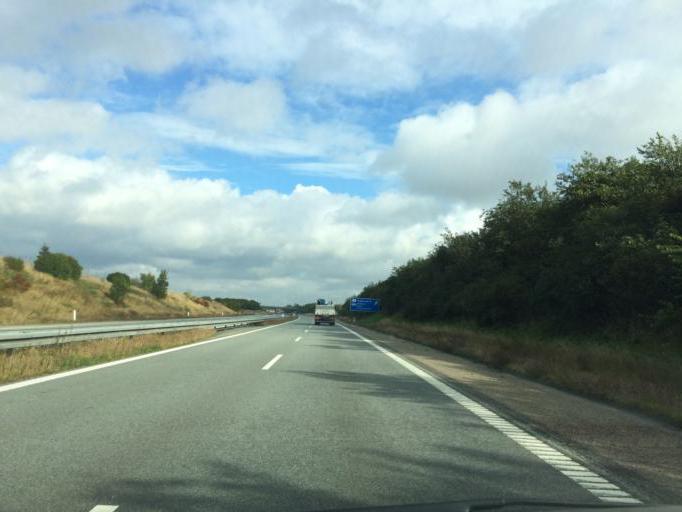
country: DK
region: North Denmark
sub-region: Bronderslev Kommune
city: Hjallerup
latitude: 57.1636
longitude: 10.1844
